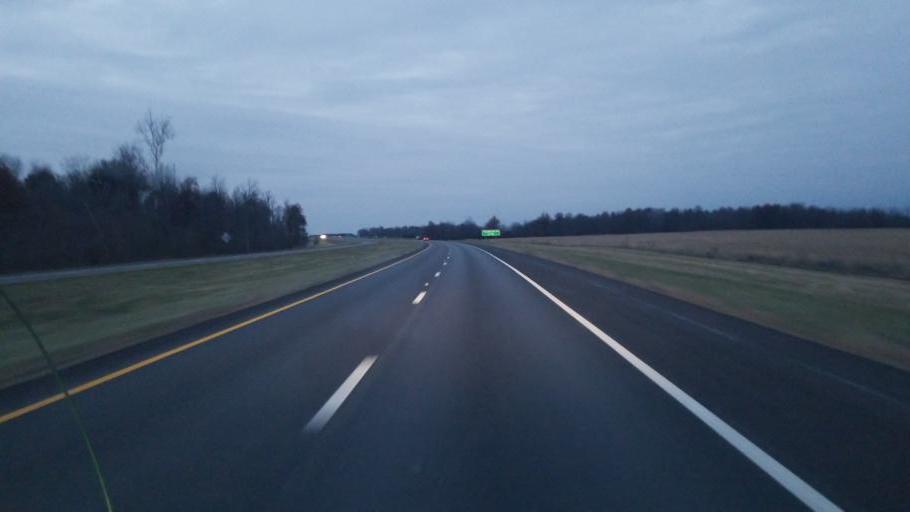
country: US
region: Ohio
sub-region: Hardin County
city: Forest
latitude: 40.8268
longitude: -83.4799
